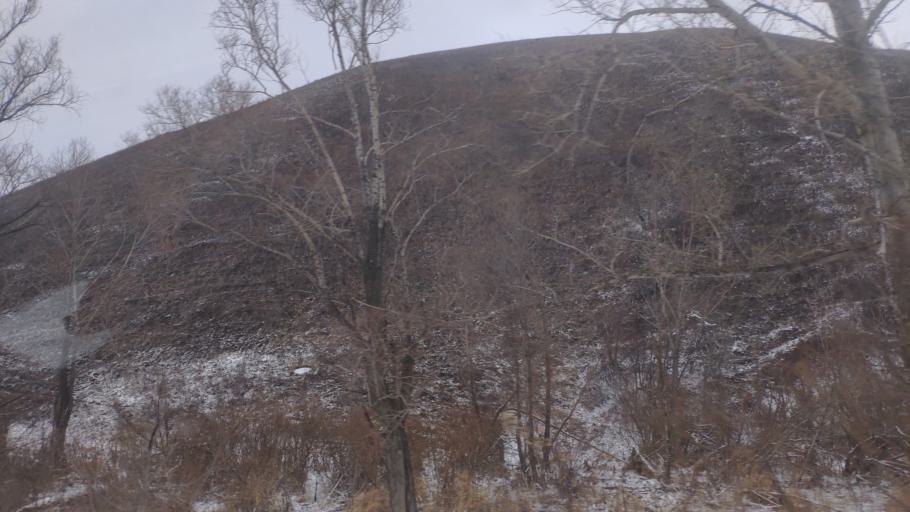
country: RU
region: Bashkortostan
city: Isyangulovo
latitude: 52.1612
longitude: 56.9174
